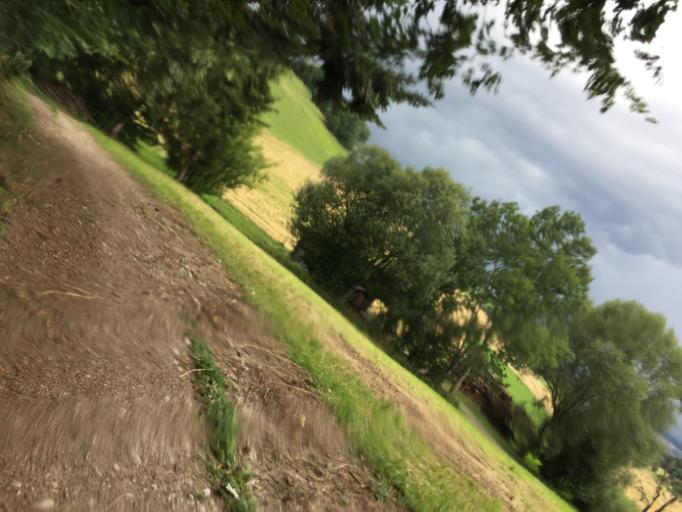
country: CH
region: Bern
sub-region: Bern-Mittelland District
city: Munsingen
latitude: 46.8574
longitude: 7.5458
